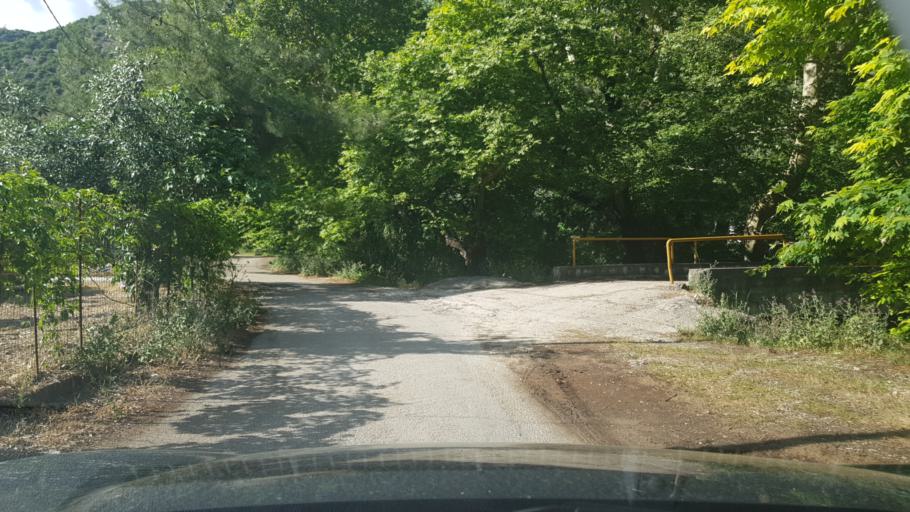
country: GR
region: Ionian Islands
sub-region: Lefkada
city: Nidri
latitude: 38.7199
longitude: 20.6952
